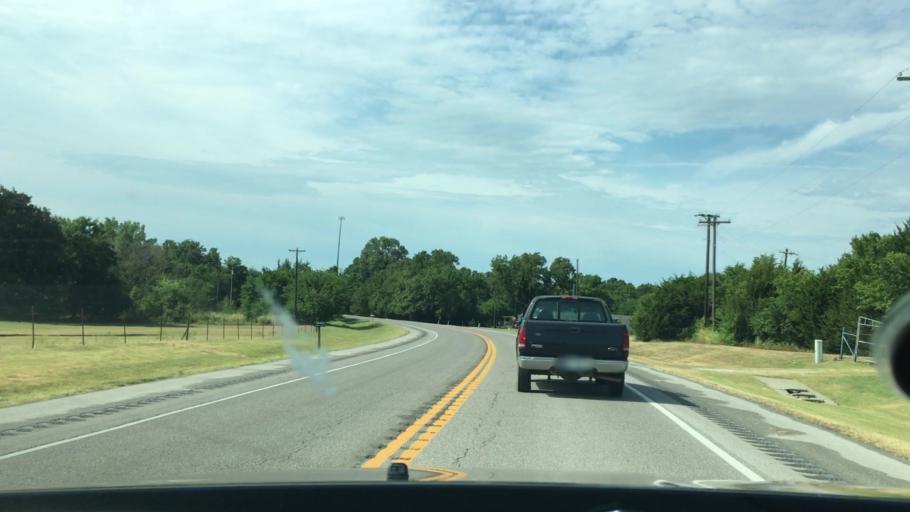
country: US
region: Oklahoma
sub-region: Murray County
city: Sulphur
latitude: 34.5275
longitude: -96.9697
